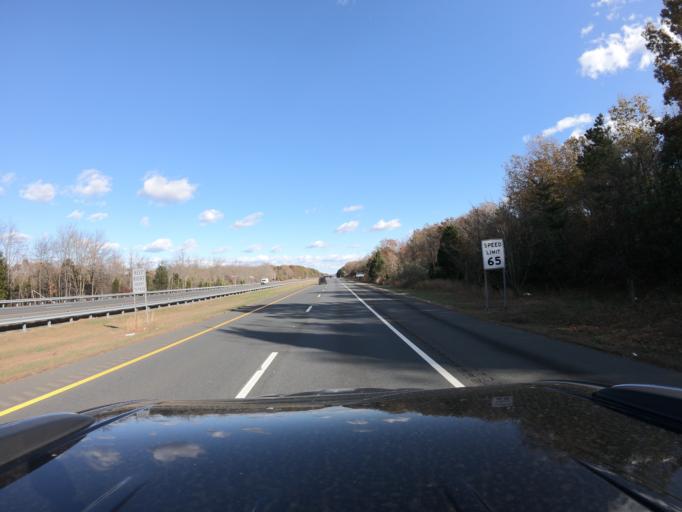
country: US
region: New Jersey
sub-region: Monmouth County
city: Farmingdale
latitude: 40.1667
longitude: -74.2204
